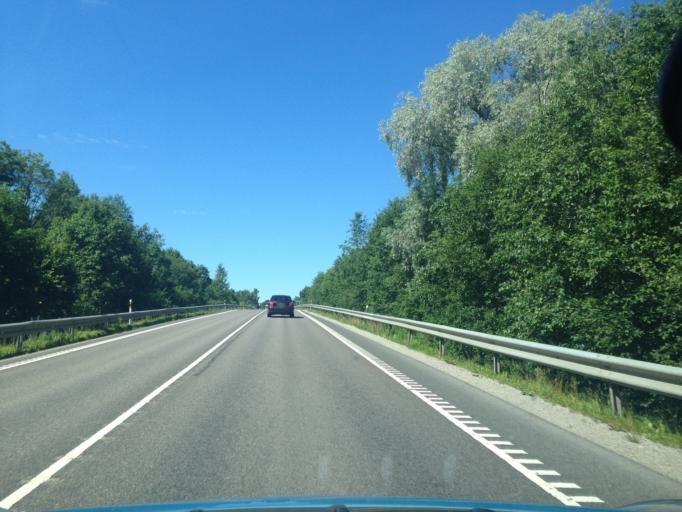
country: EE
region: Harju
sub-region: Saue linn
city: Saue
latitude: 59.3156
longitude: 24.5222
